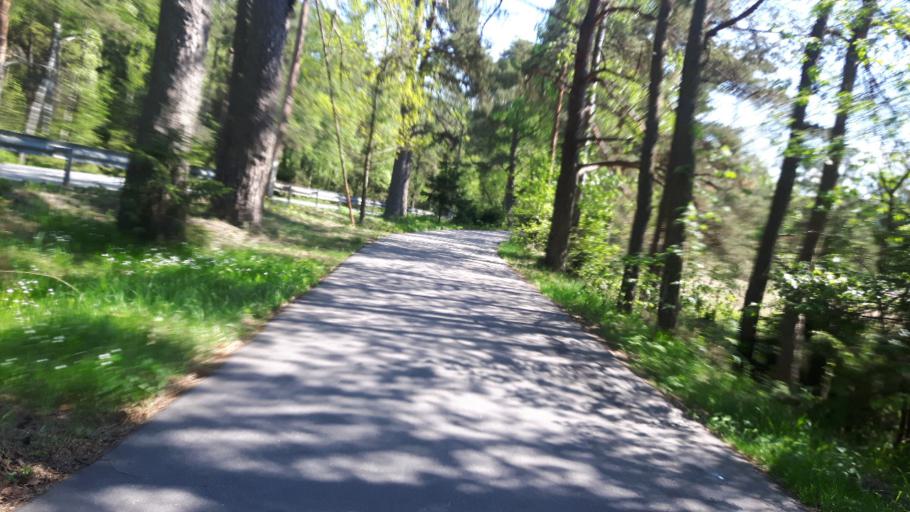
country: RU
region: St.-Petersburg
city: Komarovo
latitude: 60.1802
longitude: 29.7759
